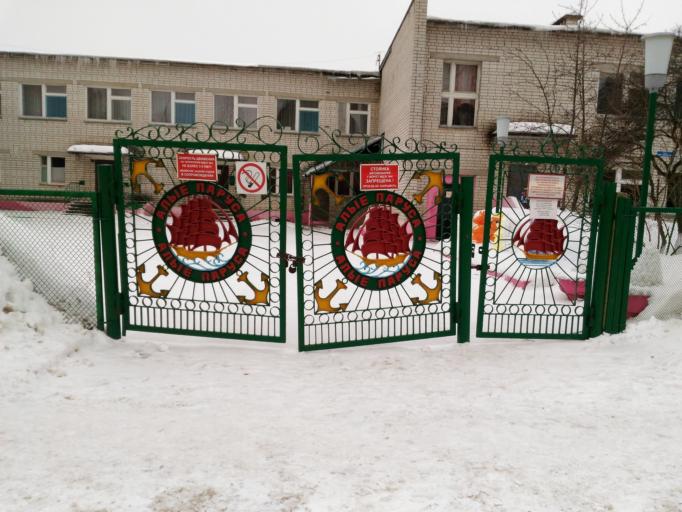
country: RU
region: Nizjnij Novgorod
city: Gorbatovka
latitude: 56.2557
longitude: 43.8501
